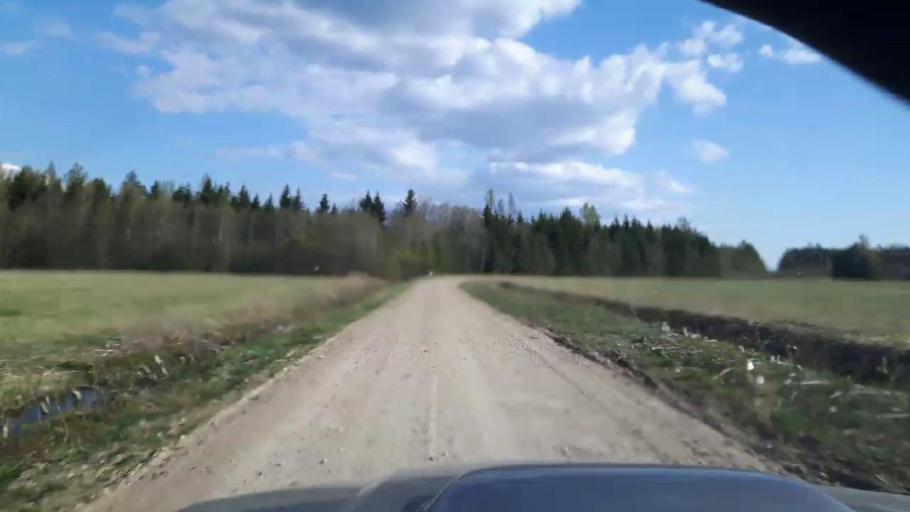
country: EE
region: Paernumaa
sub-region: Tootsi vald
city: Tootsi
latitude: 58.4318
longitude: 24.8511
